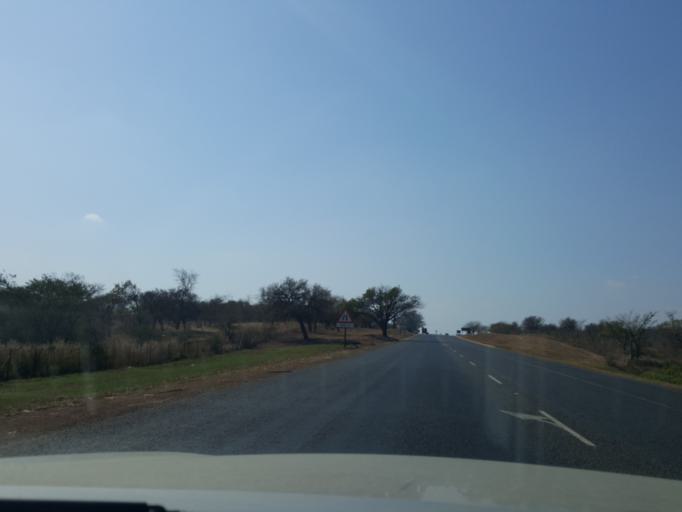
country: SZ
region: Hhohho
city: Ntfonjeni
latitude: -25.4839
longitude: 31.5429
